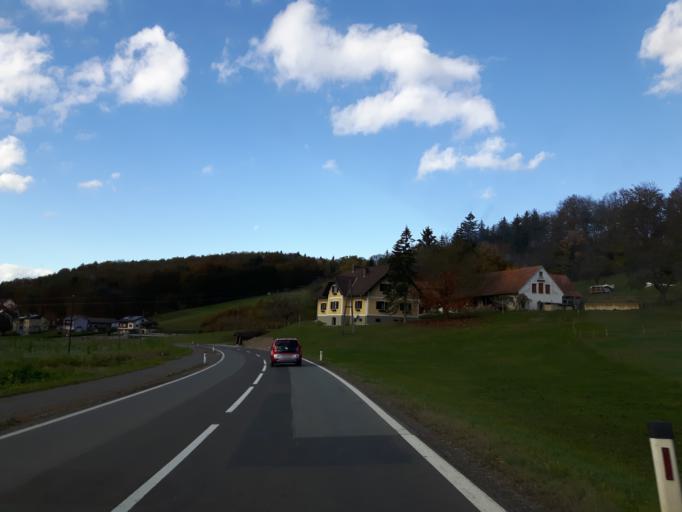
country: AT
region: Styria
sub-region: Politischer Bezirk Suedoststeiermark
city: Baumgarten bei Gnas
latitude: 46.9346
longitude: 15.7345
